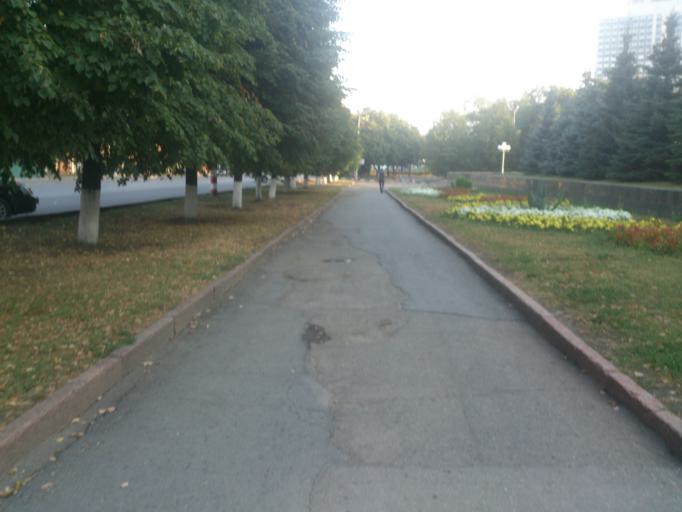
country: RU
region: Ulyanovsk
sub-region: Ulyanovskiy Rayon
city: Ulyanovsk
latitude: 54.3224
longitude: 48.4039
